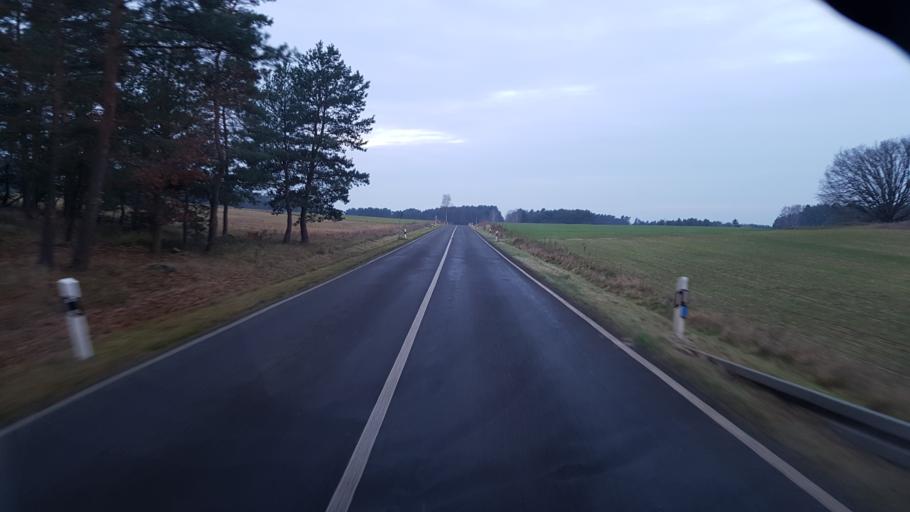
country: DE
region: Brandenburg
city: Gross Lindow
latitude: 52.1845
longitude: 14.5519
